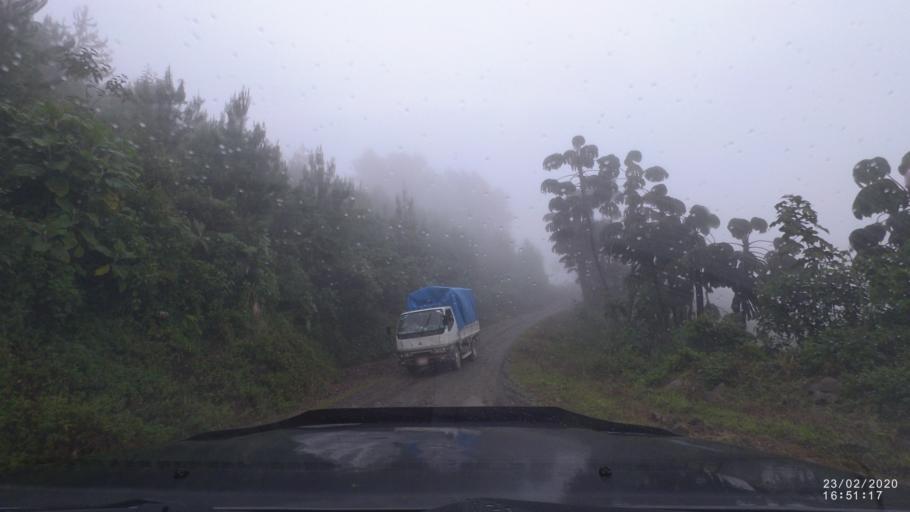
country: BO
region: Cochabamba
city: Colomi
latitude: -17.0921
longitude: -65.9838
